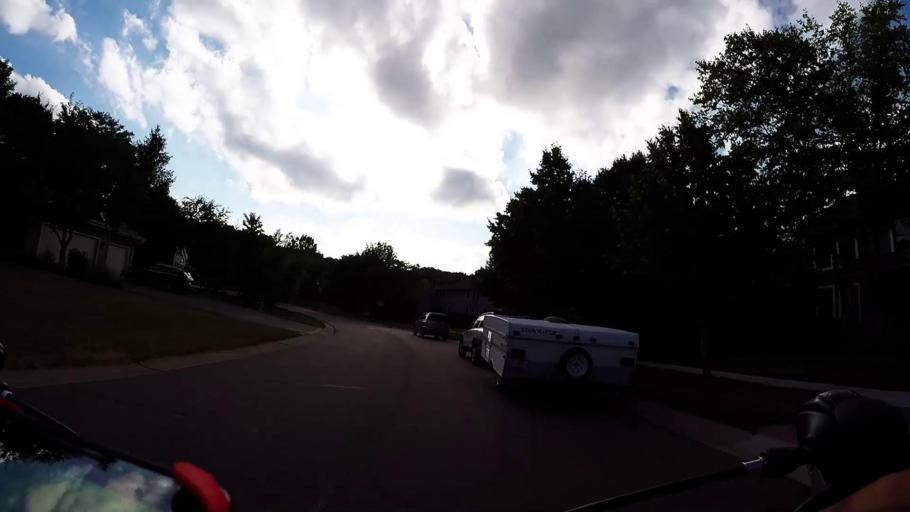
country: US
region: Minnesota
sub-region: Hennepin County
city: Minnetonka
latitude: 44.8867
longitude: -93.4853
